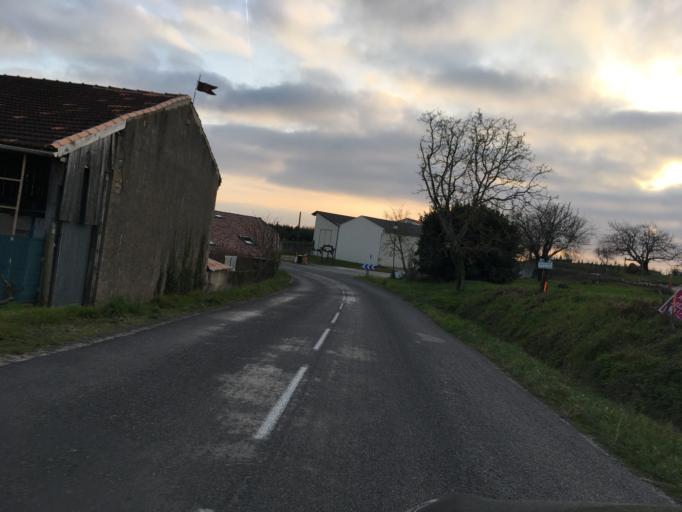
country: FR
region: Aquitaine
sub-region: Departement de la Gironde
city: Saint-Ciers-sur-Gironde
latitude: 45.3144
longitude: -0.5957
